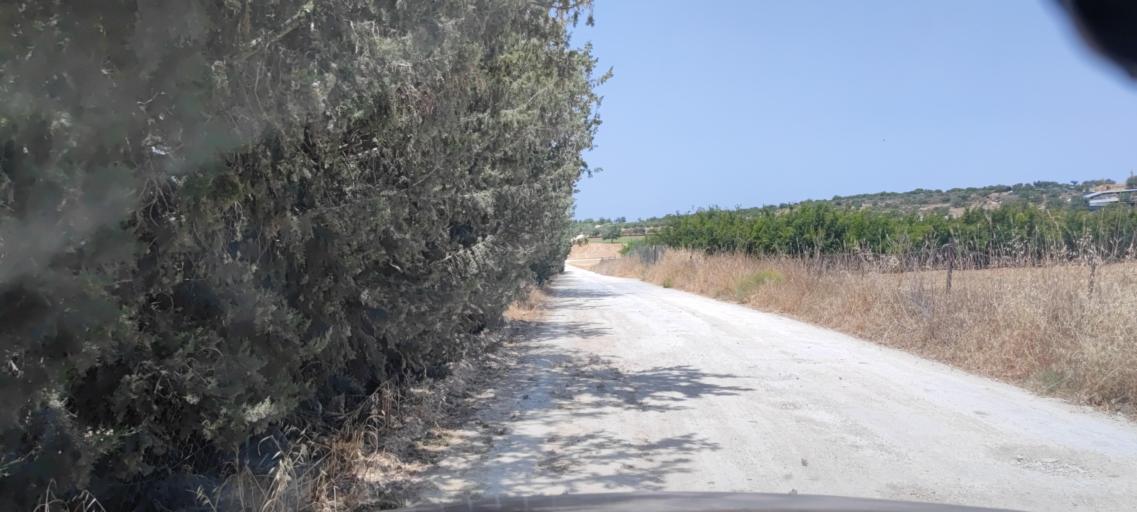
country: CY
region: Limassol
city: Pissouri
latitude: 34.7181
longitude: 32.5949
